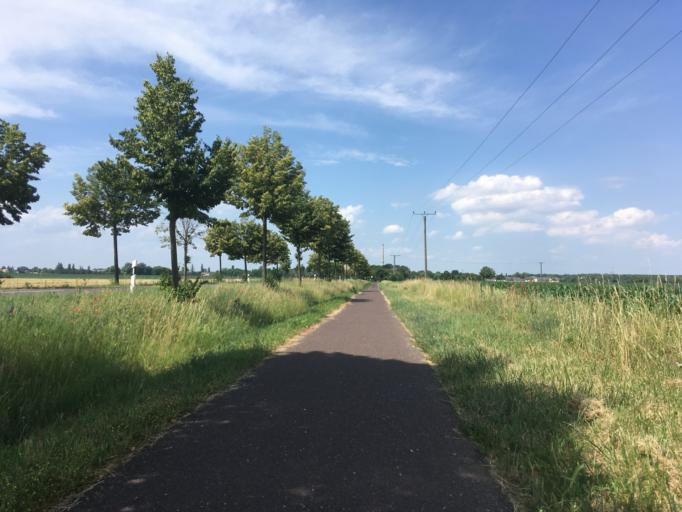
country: DE
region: Saxony-Anhalt
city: Osternienburg
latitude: 51.7529
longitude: 12.0256
